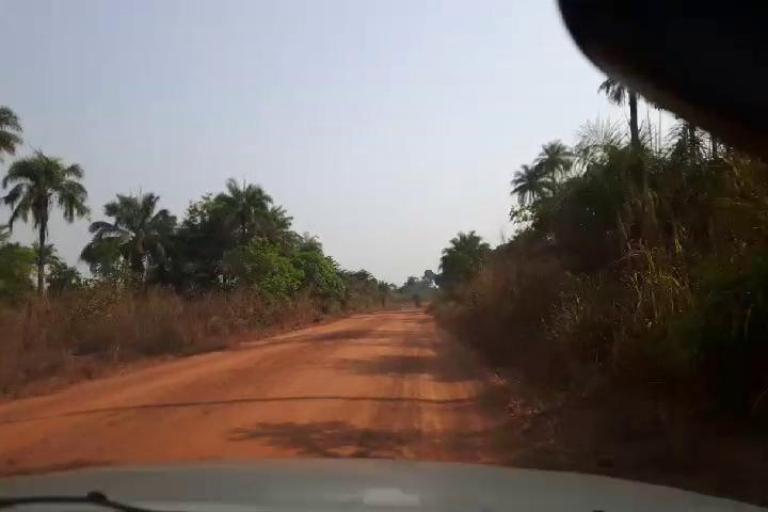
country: SL
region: Northern Province
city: Masingbi
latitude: 8.8191
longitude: -11.8594
